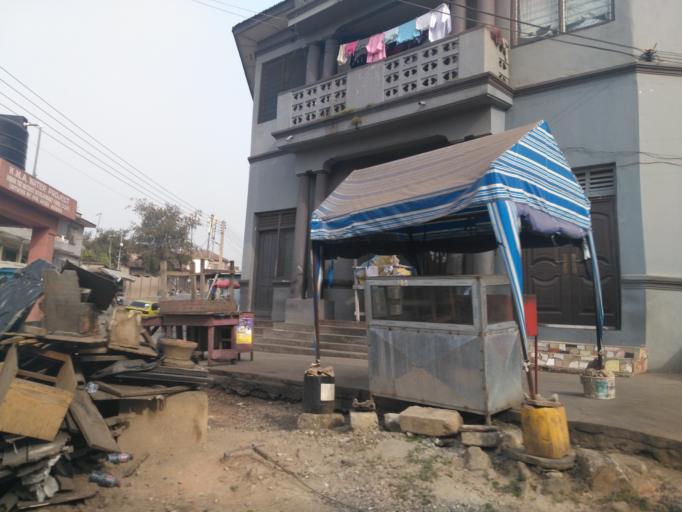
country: GH
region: Ashanti
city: Kumasi
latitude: 6.6887
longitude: -1.6117
